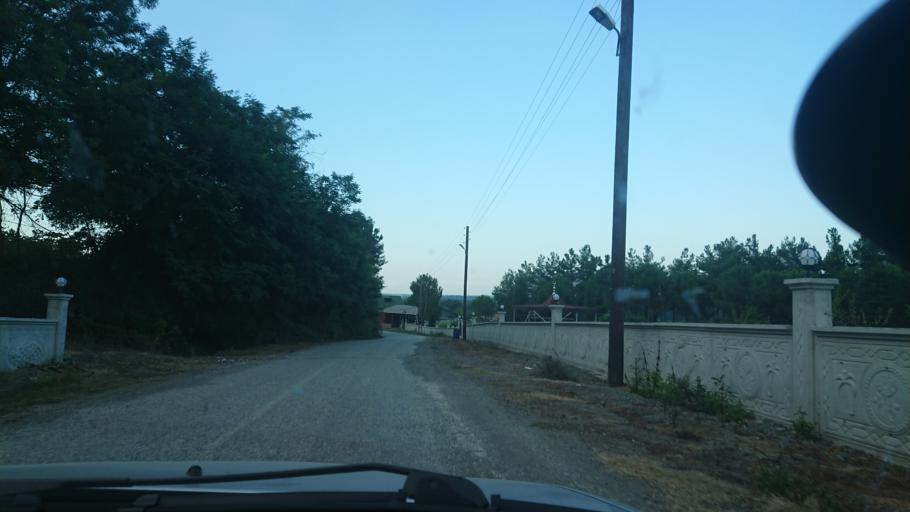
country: TR
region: Samsun
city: Dikbiyik
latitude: 41.1736
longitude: 36.5416
